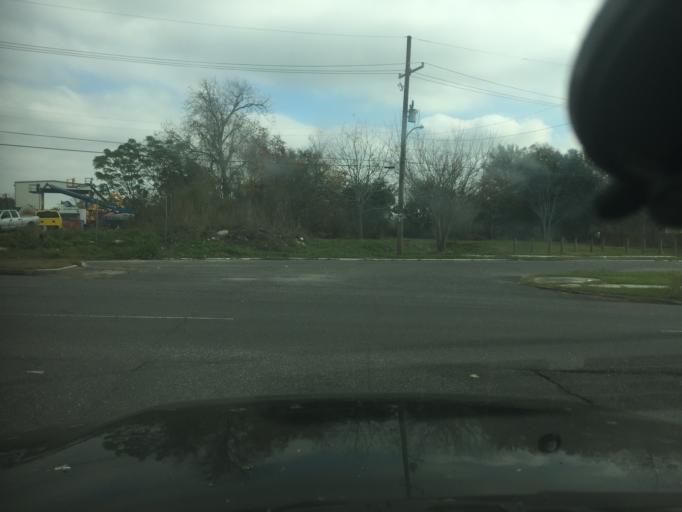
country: US
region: Louisiana
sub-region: Orleans Parish
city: New Orleans
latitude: 29.9983
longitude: -90.0412
